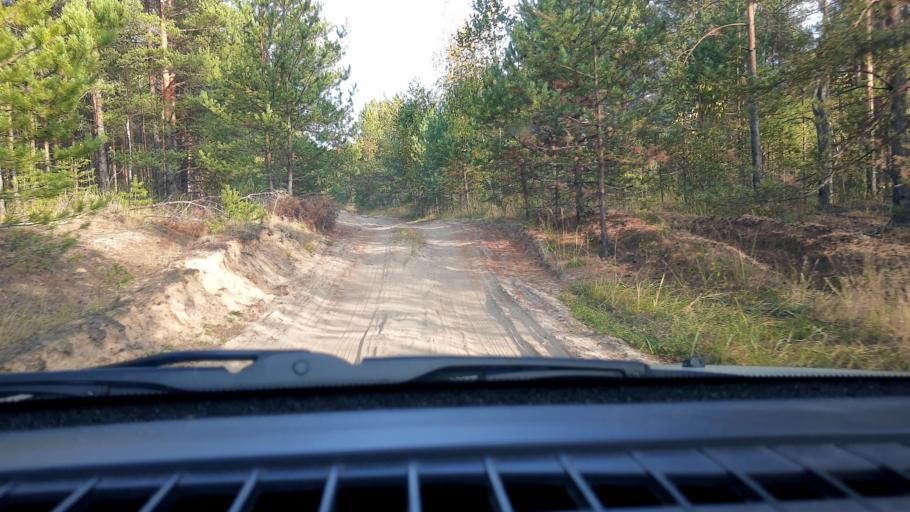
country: RU
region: Nizjnij Novgorod
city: Lukino
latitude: 56.3924
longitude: 43.6372
